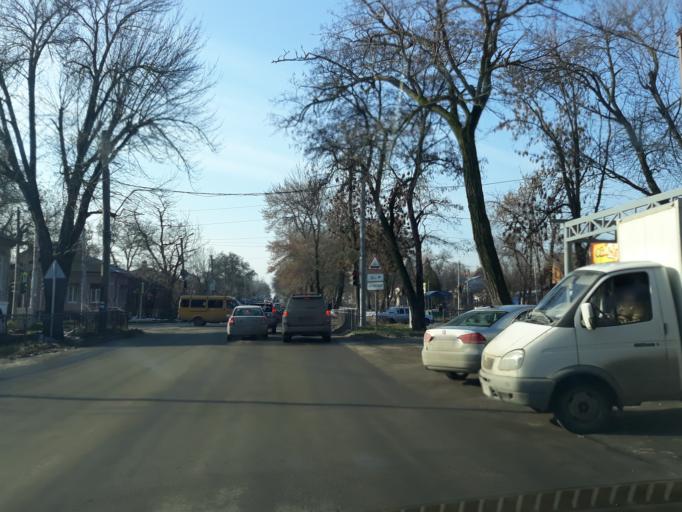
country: RU
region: Rostov
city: Taganrog
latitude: 47.2123
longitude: 38.9105
